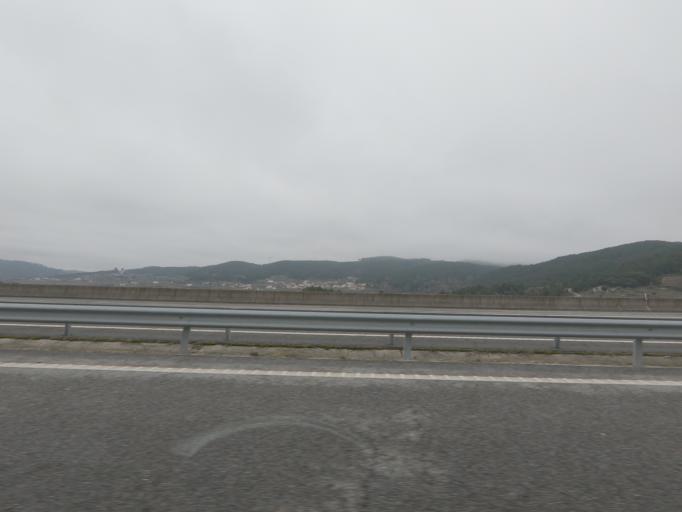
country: PT
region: Vila Real
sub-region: Boticas
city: Boticas
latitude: 41.6790
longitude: -7.5664
